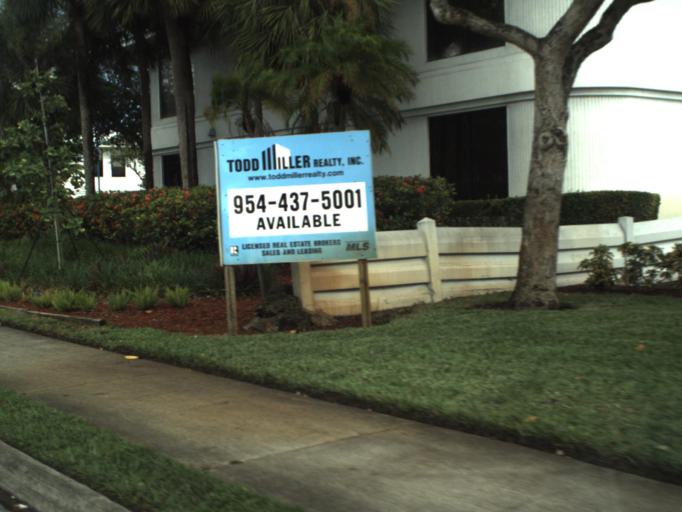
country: US
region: Florida
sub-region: Broward County
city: Carver Ranches
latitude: 26.0326
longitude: -80.1884
